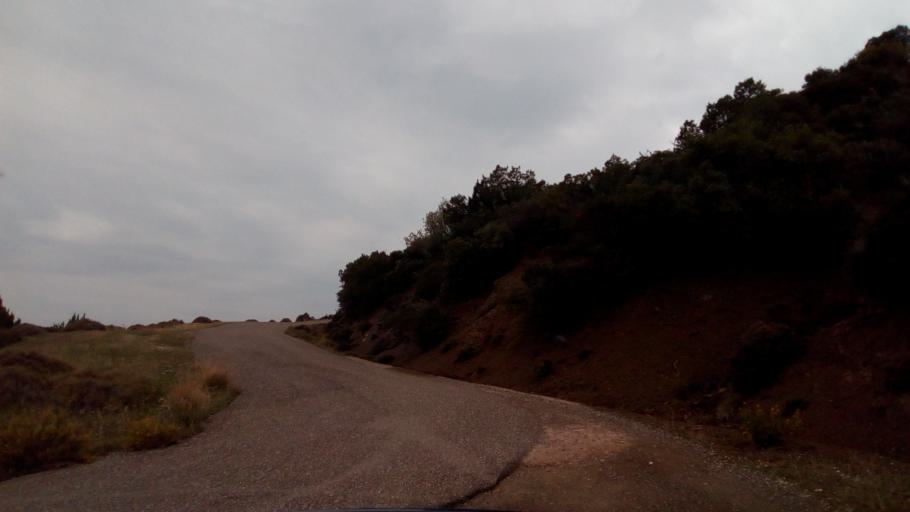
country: GR
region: West Greece
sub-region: Nomos Achaias
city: Aigio
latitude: 38.3748
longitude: 22.1525
